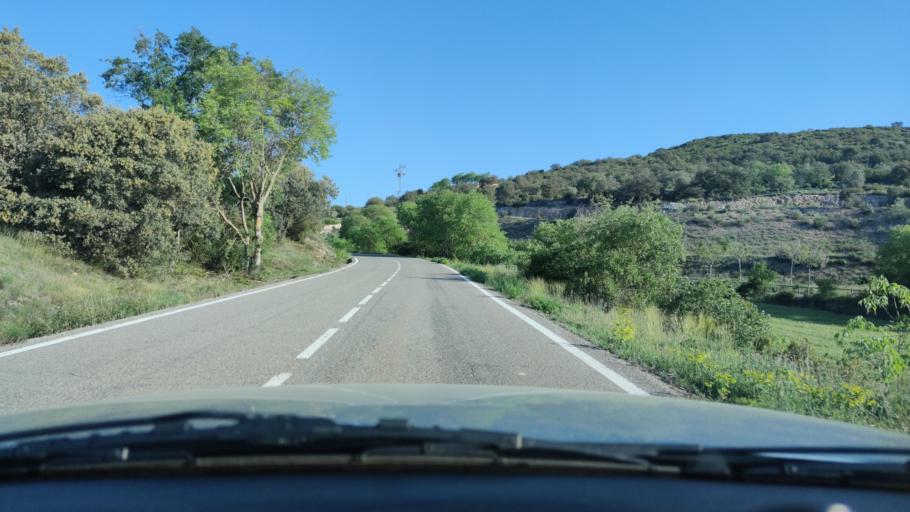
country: ES
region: Catalonia
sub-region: Provincia de Lleida
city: Artesa de Segre
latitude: 41.8793
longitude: 1.0134
